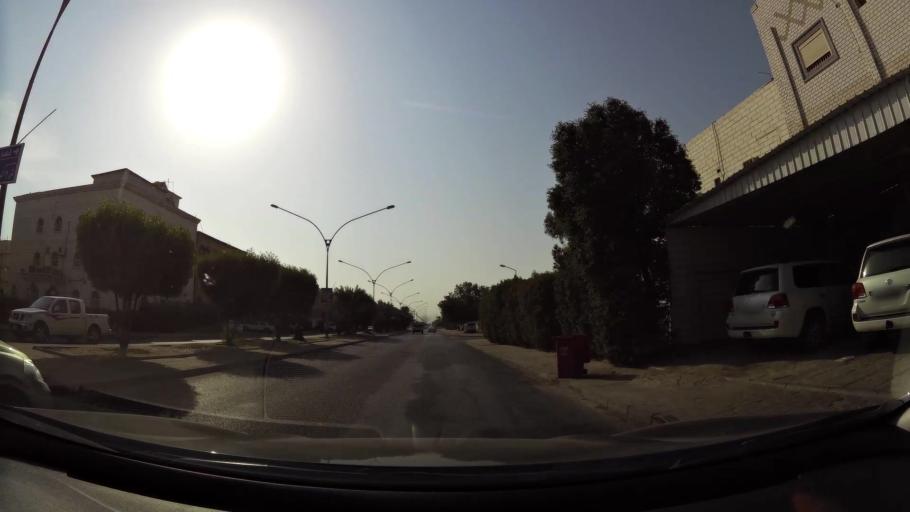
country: KW
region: Al Ahmadi
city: Ar Riqqah
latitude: 29.1606
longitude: 48.0681
